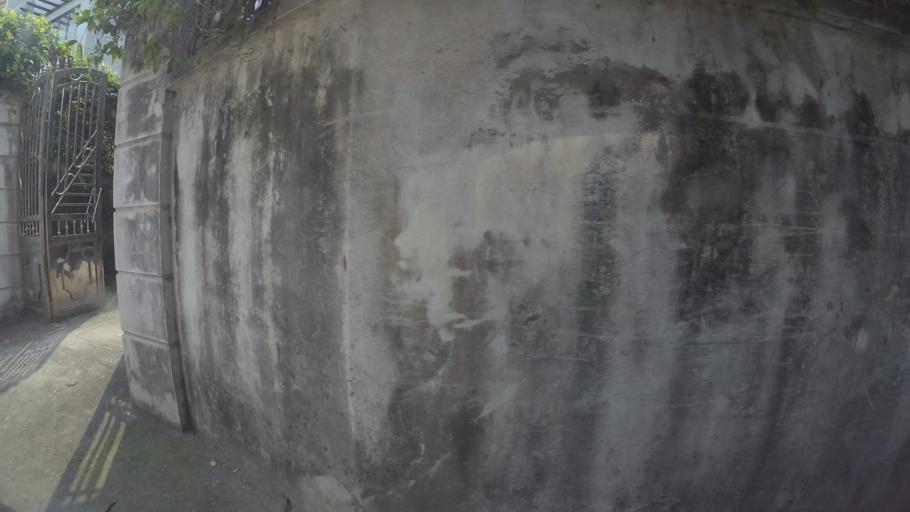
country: VN
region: Ha Noi
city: Ha Dong
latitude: 21.0008
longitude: 105.7574
